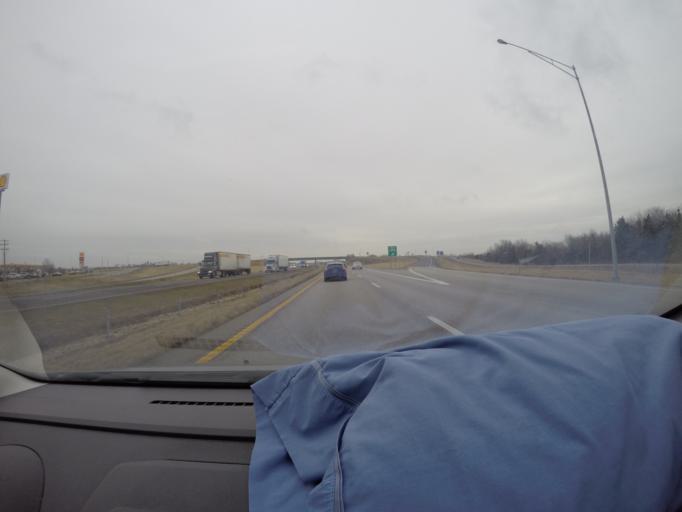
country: US
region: Missouri
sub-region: Warren County
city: Wright City
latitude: 38.8280
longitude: -91.0428
